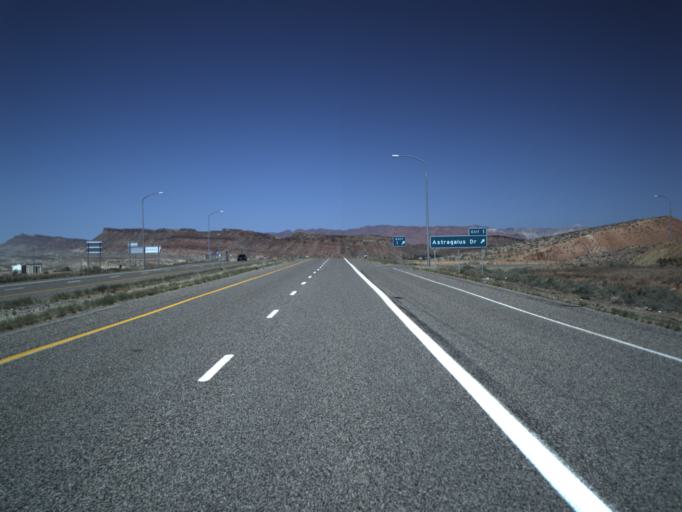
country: US
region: Utah
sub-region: Washington County
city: Saint George
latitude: 37.0228
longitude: -113.6002
